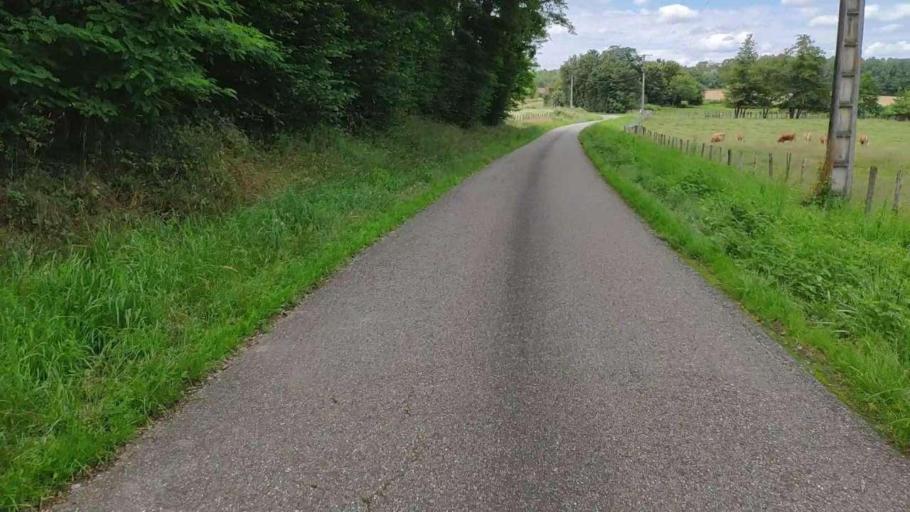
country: FR
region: Franche-Comte
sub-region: Departement du Jura
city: Chaussin
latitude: 46.8858
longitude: 5.4486
